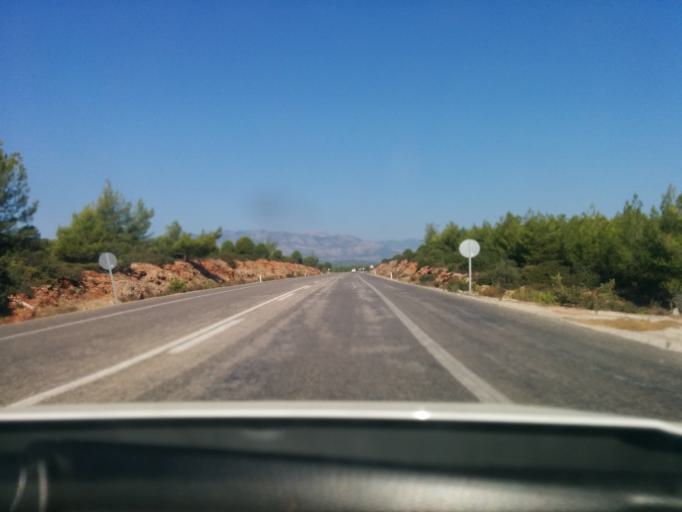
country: TR
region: Mugla
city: Esen
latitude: 36.3698
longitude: 29.3258
